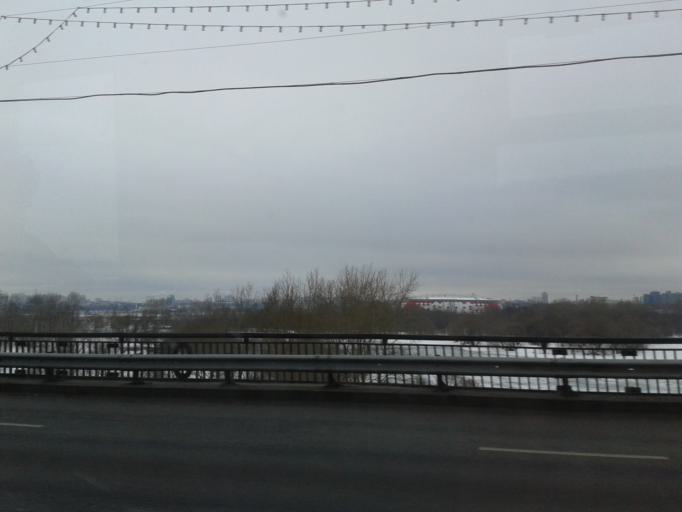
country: RU
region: Moscow
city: Shchukino
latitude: 55.8053
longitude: 37.4451
